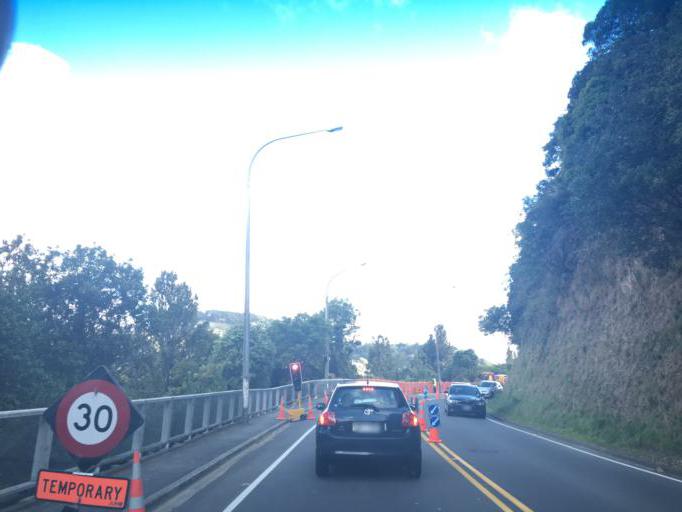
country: NZ
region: Wellington
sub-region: Wellington City
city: Kelburn
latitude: -41.2570
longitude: 174.7750
